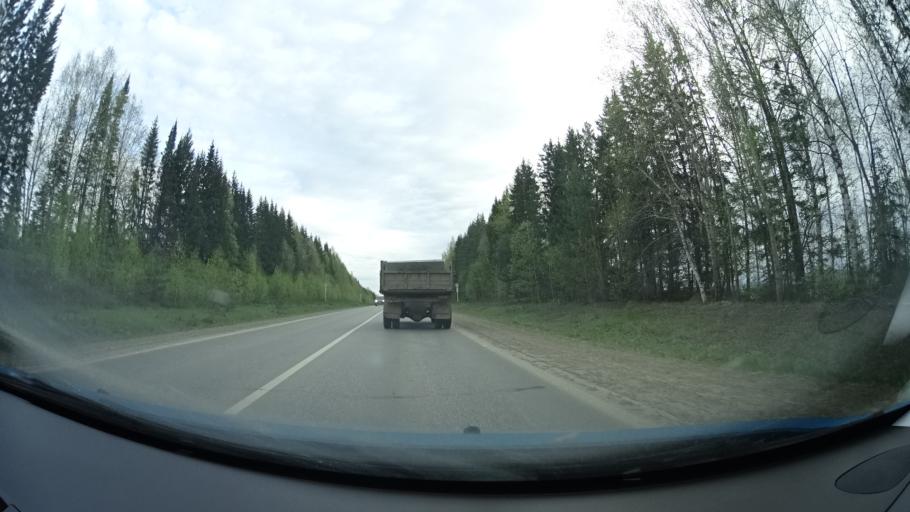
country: RU
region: Perm
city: Osa
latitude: 57.4073
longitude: 55.6232
